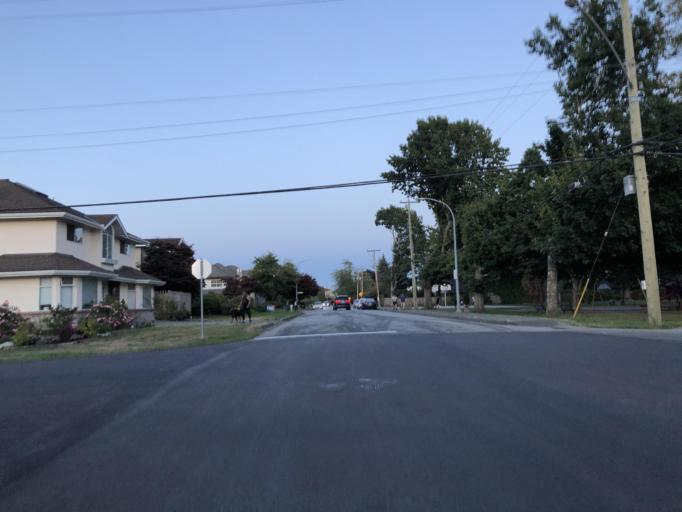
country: CA
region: British Columbia
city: Richmond
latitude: 49.1501
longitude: -123.1228
